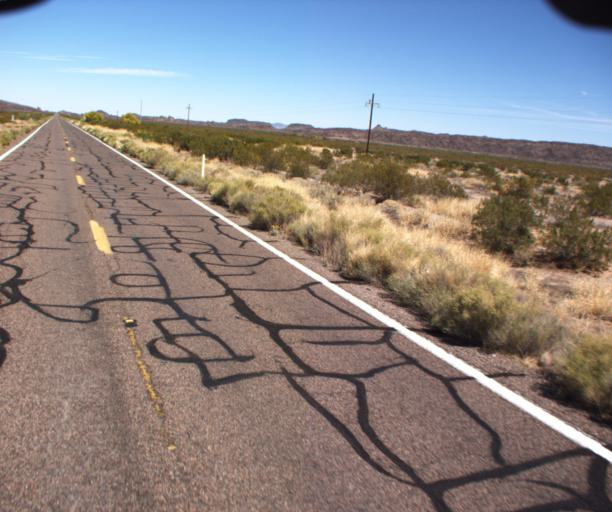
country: US
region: Arizona
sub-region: Pima County
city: Ajo
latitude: 32.5122
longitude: -112.8808
